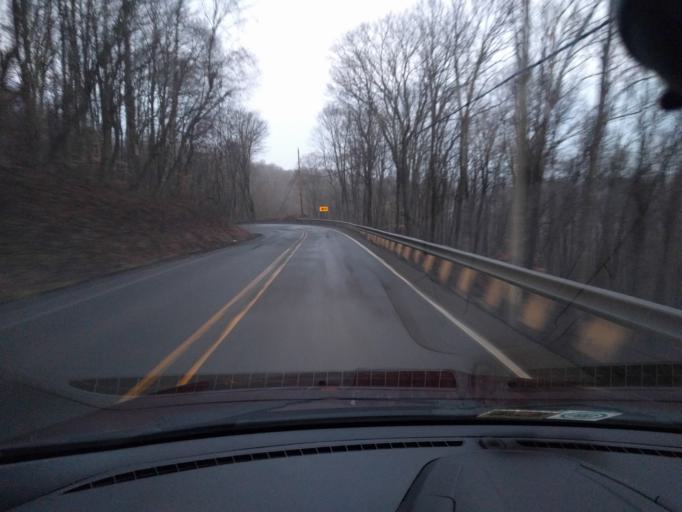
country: US
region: West Virginia
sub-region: Greenbrier County
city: Rainelle
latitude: 37.9861
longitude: -80.8509
